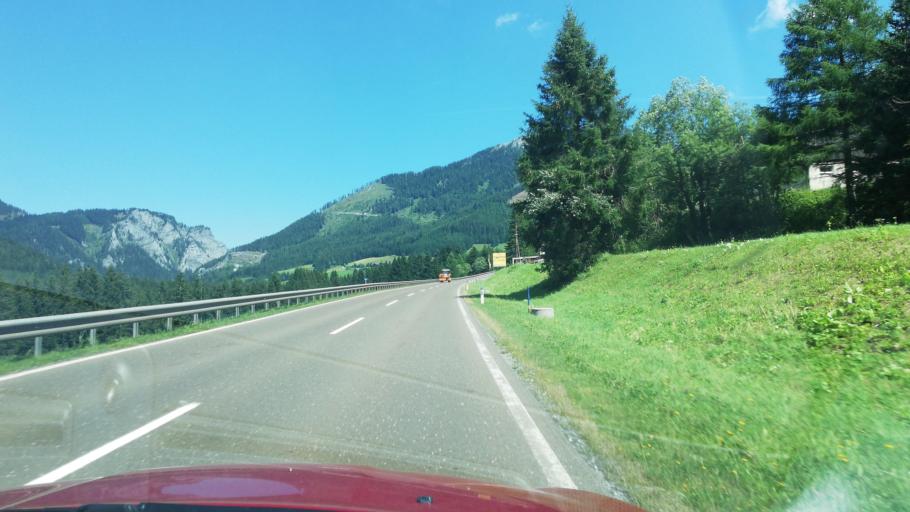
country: AT
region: Styria
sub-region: Politischer Bezirk Murtal
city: Hohentauern
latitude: 47.4268
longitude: 14.4638
